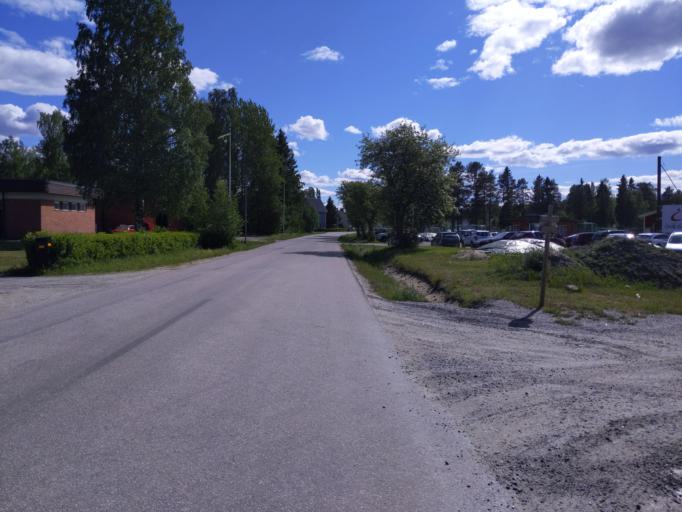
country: SE
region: Vaesternorrland
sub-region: OErnskoeldsviks Kommun
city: Kopmanholmen
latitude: 63.1717
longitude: 18.5669
